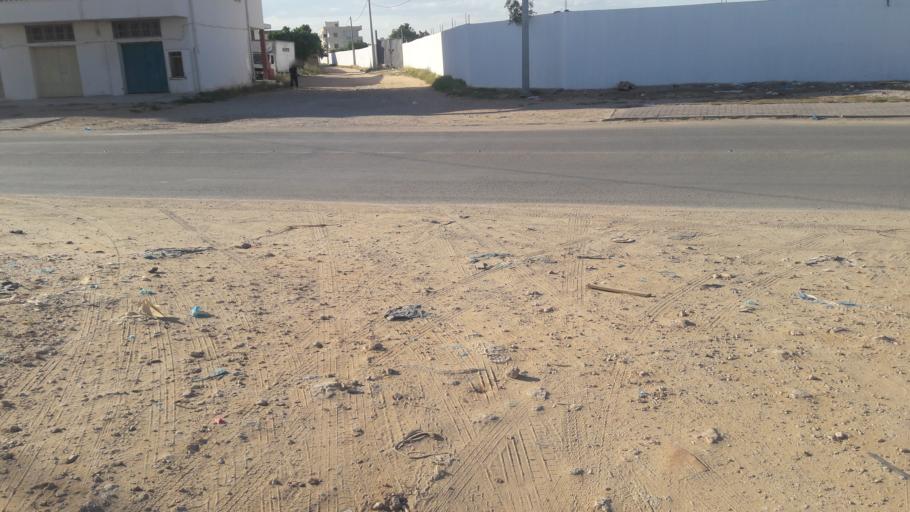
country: TN
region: Safaqis
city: Sfax
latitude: 34.8150
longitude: 10.7405
